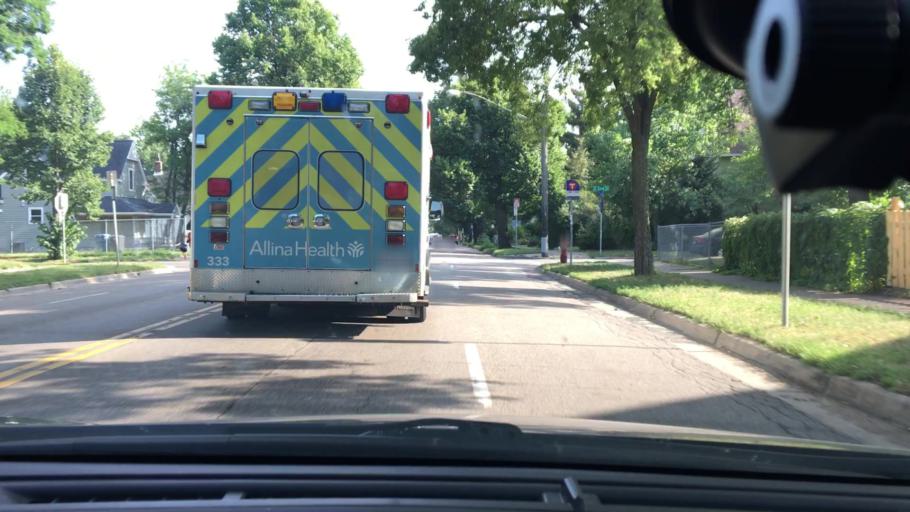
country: US
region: Minnesota
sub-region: Hennepin County
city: Minneapolis
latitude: 44.9433
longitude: -93.2474
